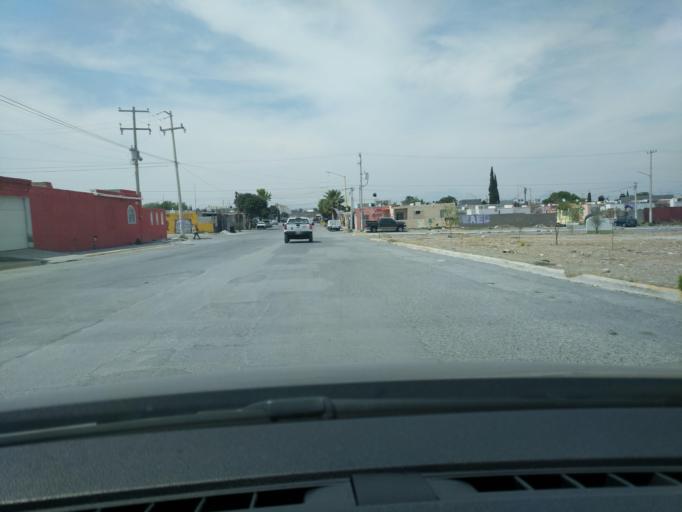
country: MX
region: Coahuila
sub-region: Arteaga
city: Arteaga
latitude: 25.4280
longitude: -100.9092
